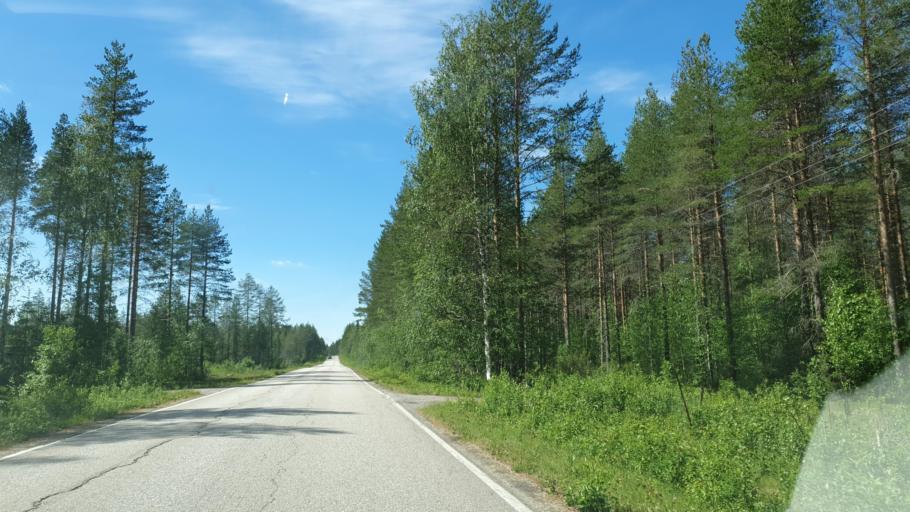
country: FI
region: Kainuu
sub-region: Kehys-Kainuu
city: Suomussalmi
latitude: 64.5831
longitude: 29.0511
